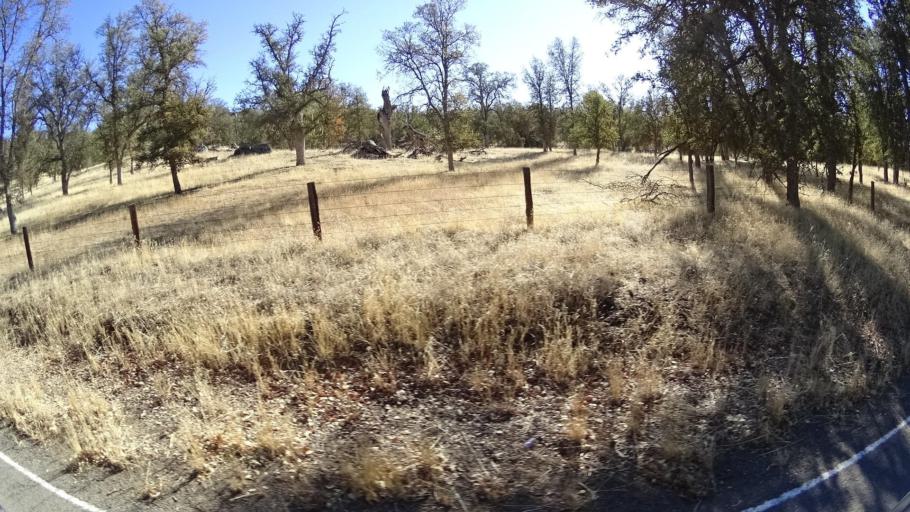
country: US
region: California
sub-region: Kern County
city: Alta Sierra
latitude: 35.7485
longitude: -118.7170
